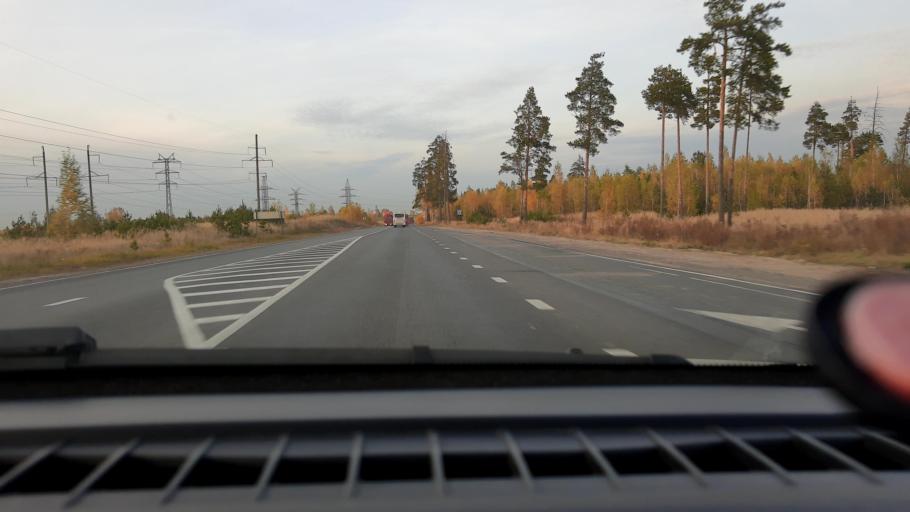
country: RU
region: Nizjnij Novgorod
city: Babino
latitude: 56.3228
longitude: 43.5591
